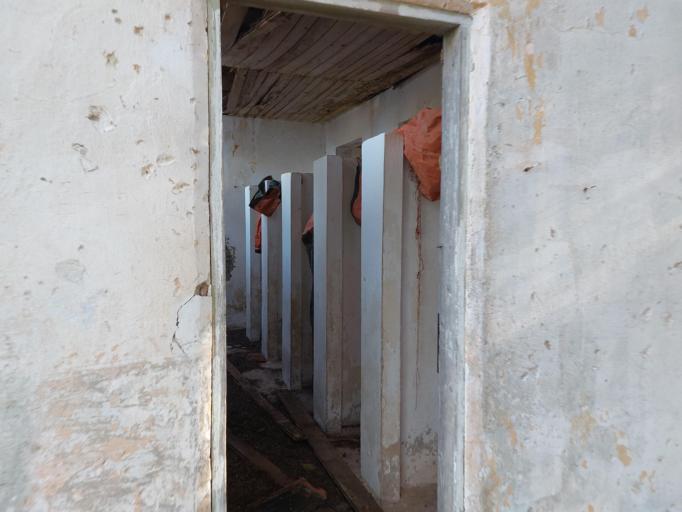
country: HR
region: Dubrovacko-Neretvanska
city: Smokvica
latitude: 42.7704
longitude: 16.7912
